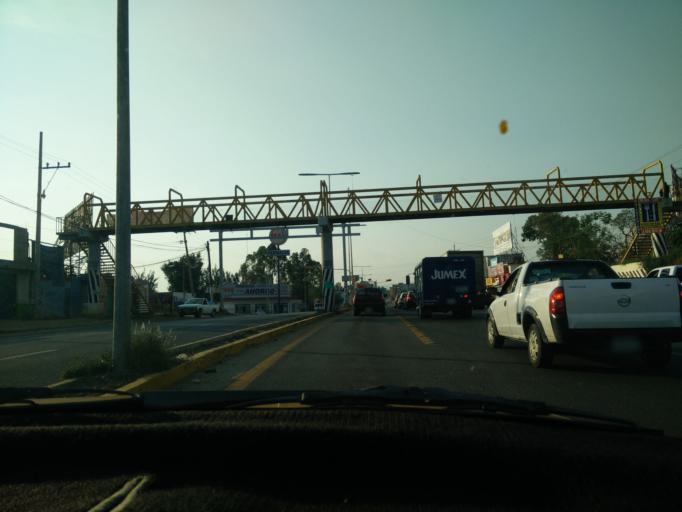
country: MX
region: Oaxaca
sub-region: San Lorenzo Cacaotepec
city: Santiago Etla
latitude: 17.1357
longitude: -96.7748
